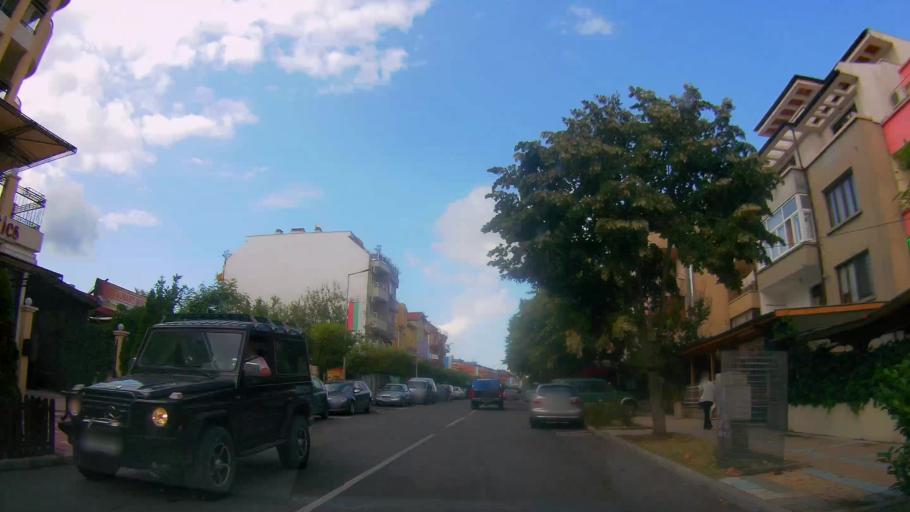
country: BG
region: Burgas
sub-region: Obshtina Primorsko
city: Primorsko
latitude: 42.2667
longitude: 27.7493
